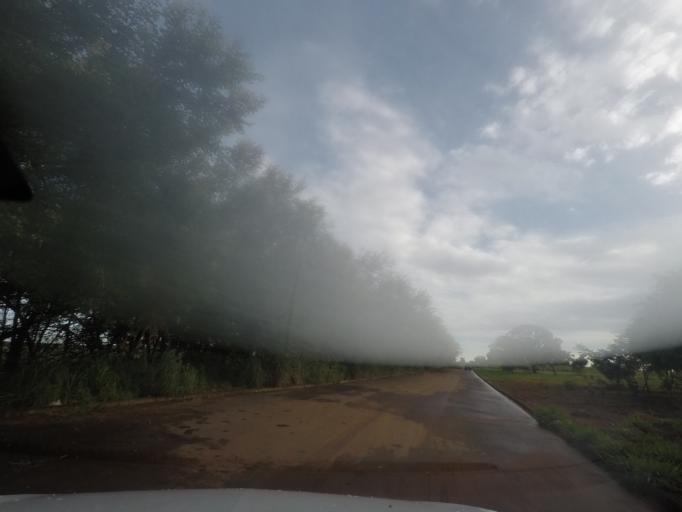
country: BR
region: Goias
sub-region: Aparecida De Goiania
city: Aparecida de Goiania
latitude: -16.7761
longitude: -49.3889
